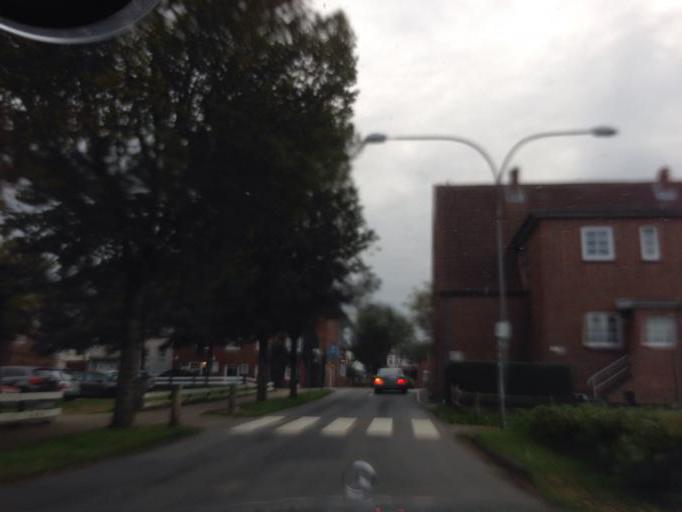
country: DE
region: Schleswig-Holstein
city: Wyk auf Fohr
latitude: 54.6918
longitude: 8.5677
